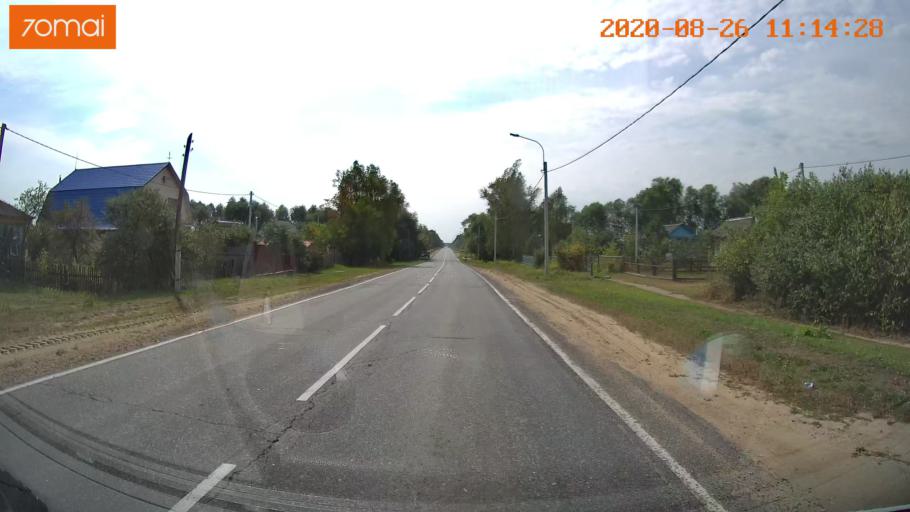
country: RU
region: Rjazan
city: Izhevskoye
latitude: 54.4488
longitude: 41.1168
